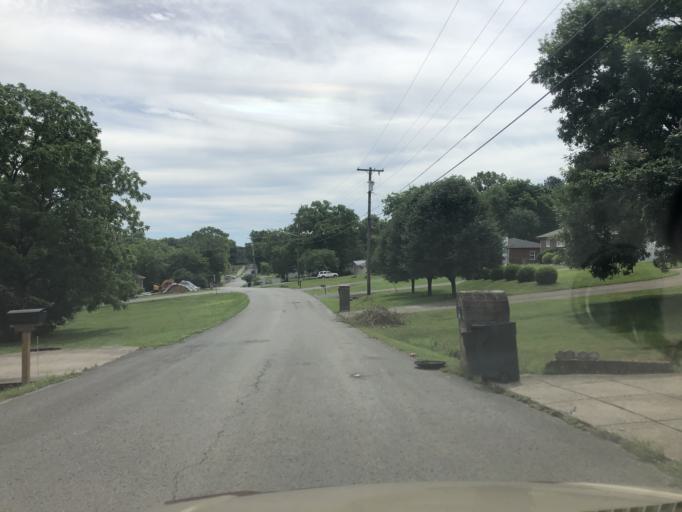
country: US
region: Tennessee
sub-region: Davidson County
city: Lakewood
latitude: 36.2592
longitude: -86.6128
